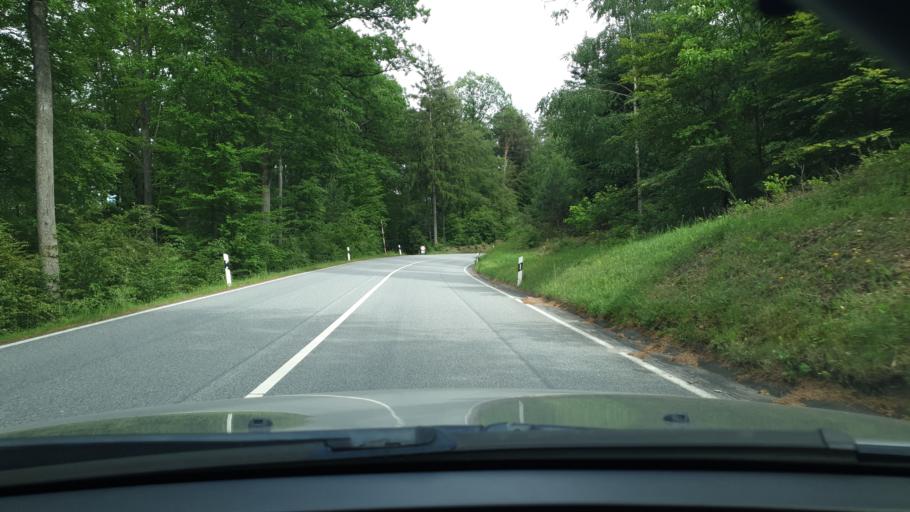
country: DE
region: Rheinland-Pfalz
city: Waldleiningen
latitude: 49.3983
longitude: 7.8489
